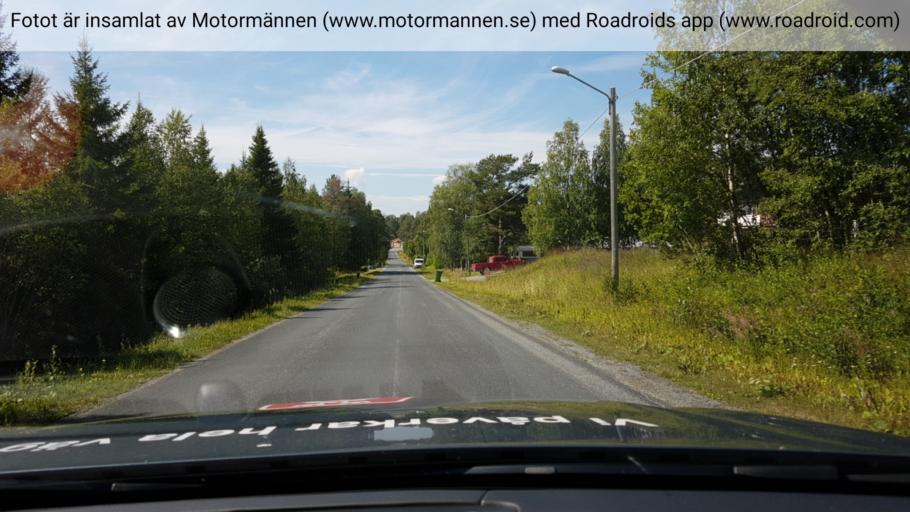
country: SE
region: Jaemtland
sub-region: Krokoms Kommun
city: Valla
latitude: 63.3028
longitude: 13.8422
